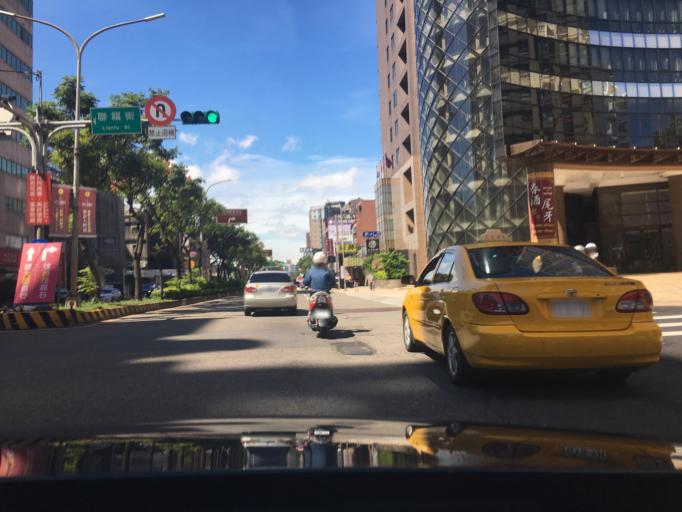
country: TW
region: Taiwan
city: Taoyuan City
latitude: 25.0515
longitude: 121.2886
